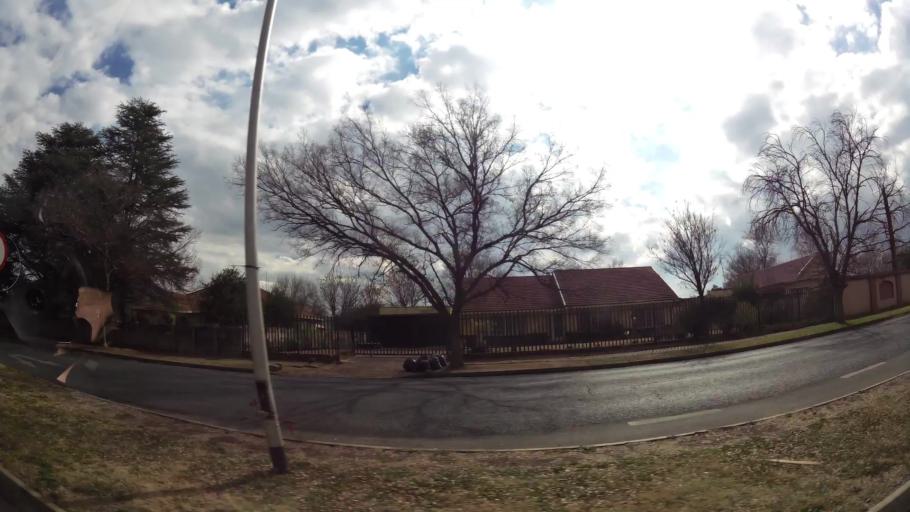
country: ZA
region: Gauteng
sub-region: Sedibeng District Municipality
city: Vereeniging
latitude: -26.6607
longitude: 27.9819
